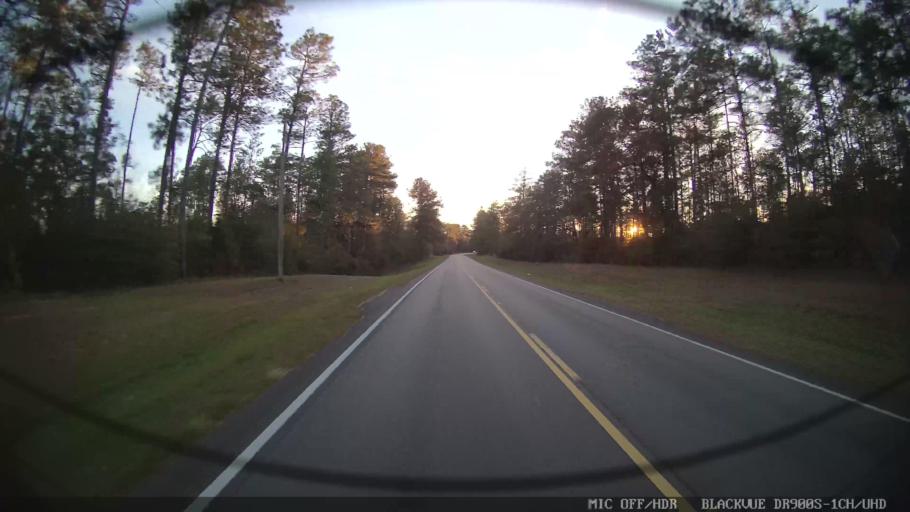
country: US
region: Mississippi
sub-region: Stone County
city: Wiggins
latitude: 31.0364
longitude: -89.2169
